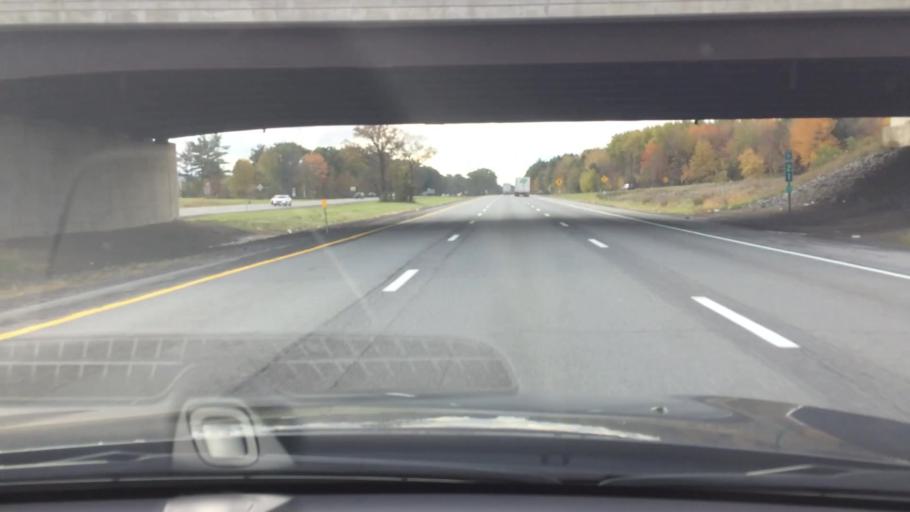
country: US
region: New York
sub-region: Saratoga County
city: Country Knolls
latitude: 42.9706
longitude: -73.8022
